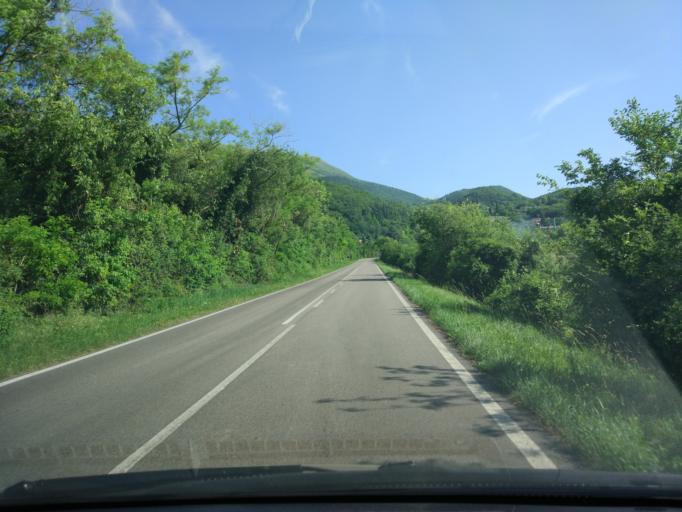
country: IT
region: Veneto
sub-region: Provincia di Verona
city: Caprino Veronese
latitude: 45.6124
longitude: 10.8166
